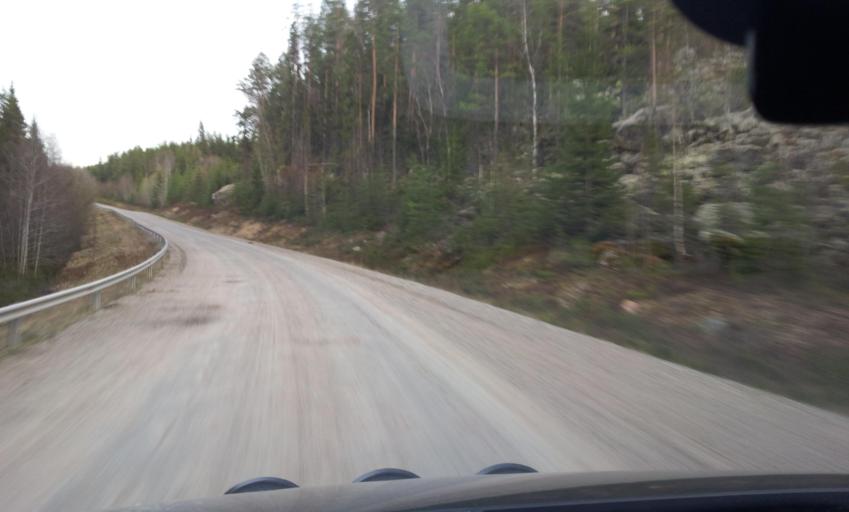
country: SE
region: Gaevleborg
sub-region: Ljusdals Kommun
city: Farila
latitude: 62.0251
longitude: 15.8230
